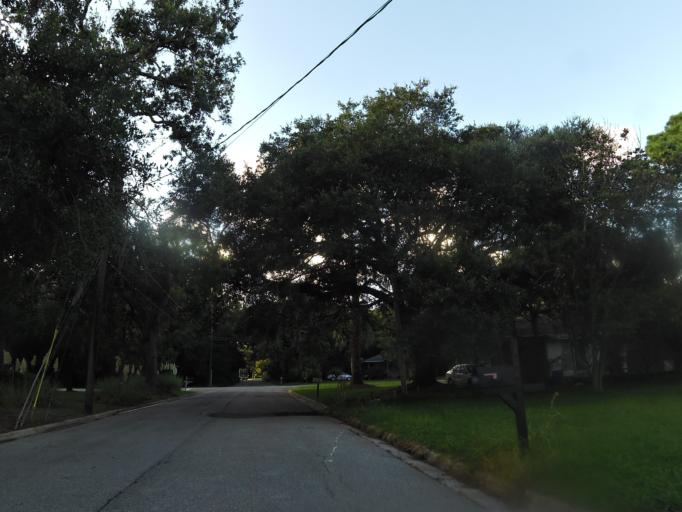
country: US
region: Georgia
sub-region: Glynn County
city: Brunswick
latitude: 31.1309
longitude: -81.4877
